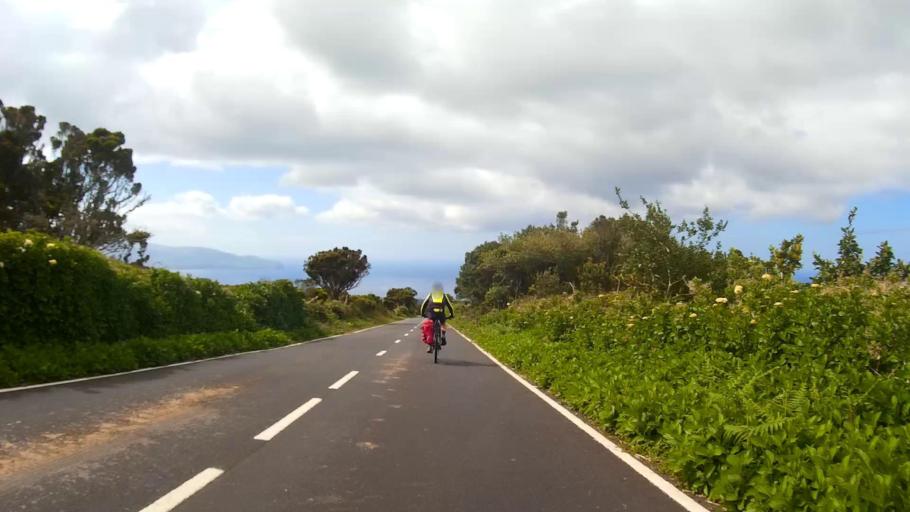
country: PT
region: Azores
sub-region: Madalena
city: Madalena
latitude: 38.4975
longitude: -28.4614
